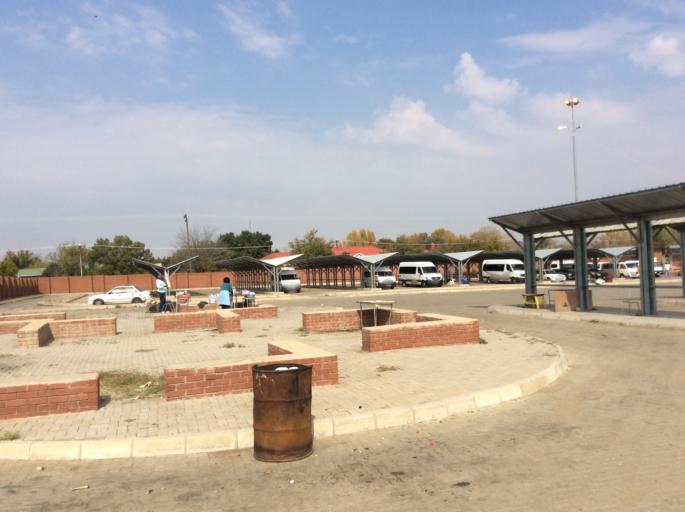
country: LS
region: Mafeteng
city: Mafeteng
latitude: -29.7295
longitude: 27.0374
